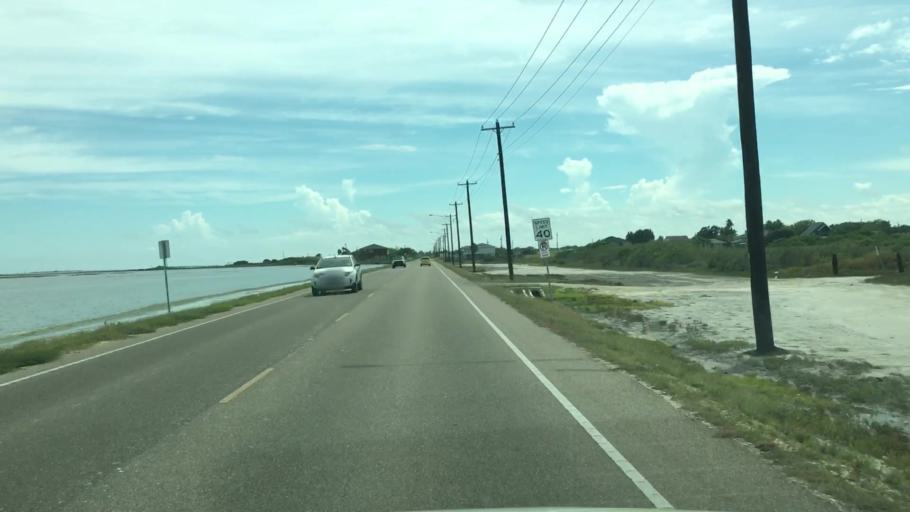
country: US
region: Texas
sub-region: Nueces County
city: Corpus Christi
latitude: 27.6508
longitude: -97.2802
